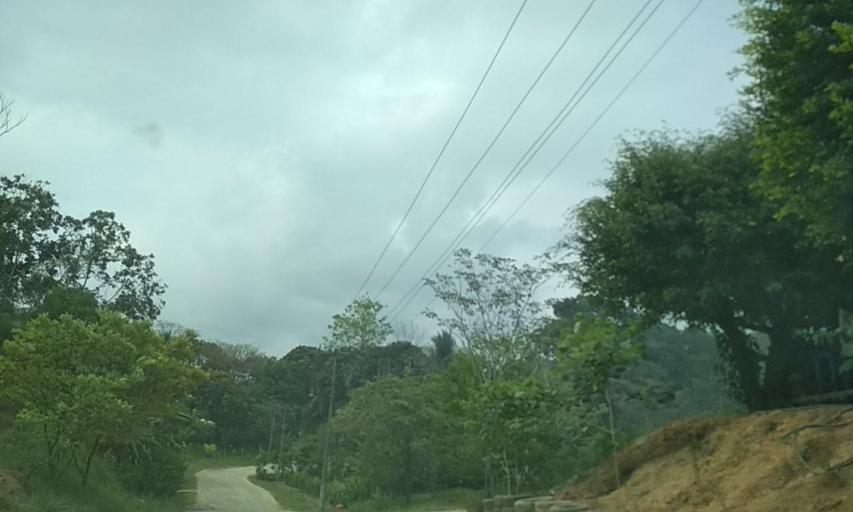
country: MX
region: Veracruz
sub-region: Uxpanapa
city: Poblado 10
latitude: 17.4569
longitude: -94.1016
